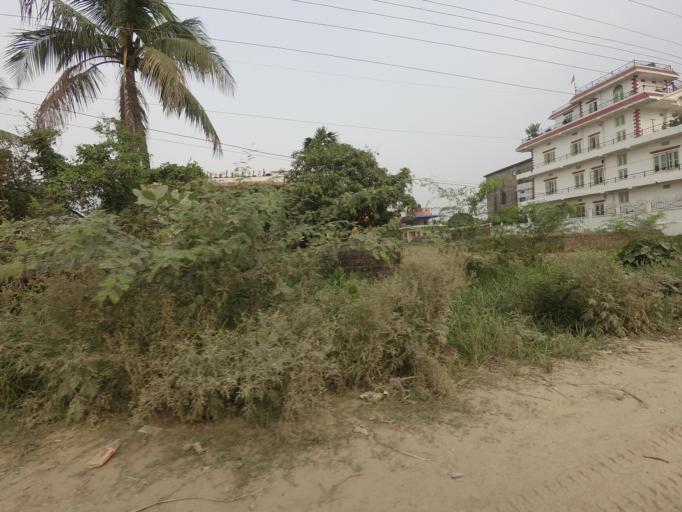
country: NP
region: Western Region
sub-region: Lumbini Zone
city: Bhairahawa
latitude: 27.5178
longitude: 83.4417
